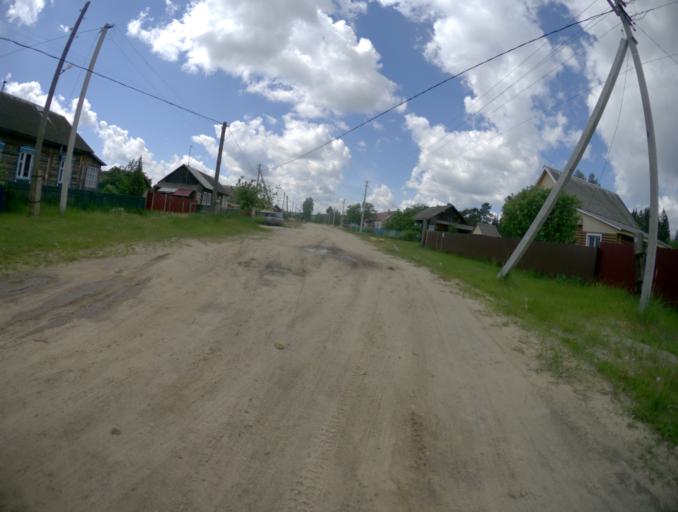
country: RU
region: Vladimir
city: Velikodvorskiy
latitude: 55.2370
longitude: 40.6480
